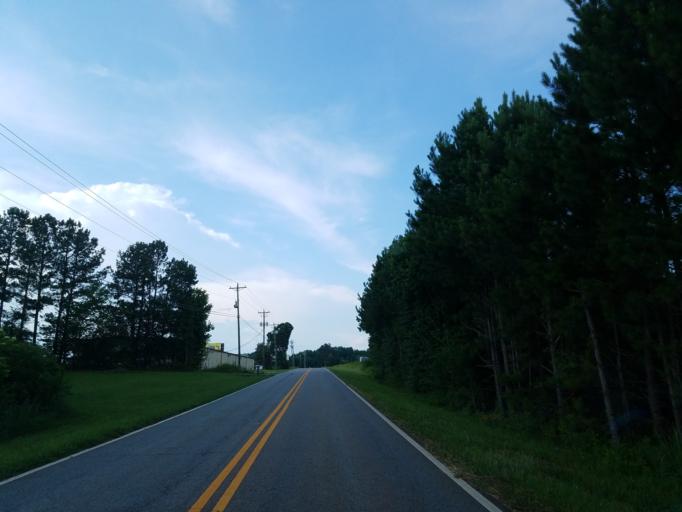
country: US
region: Georgia
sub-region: Forsyth County
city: Cumming
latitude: 34.3079
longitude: -84.0660
